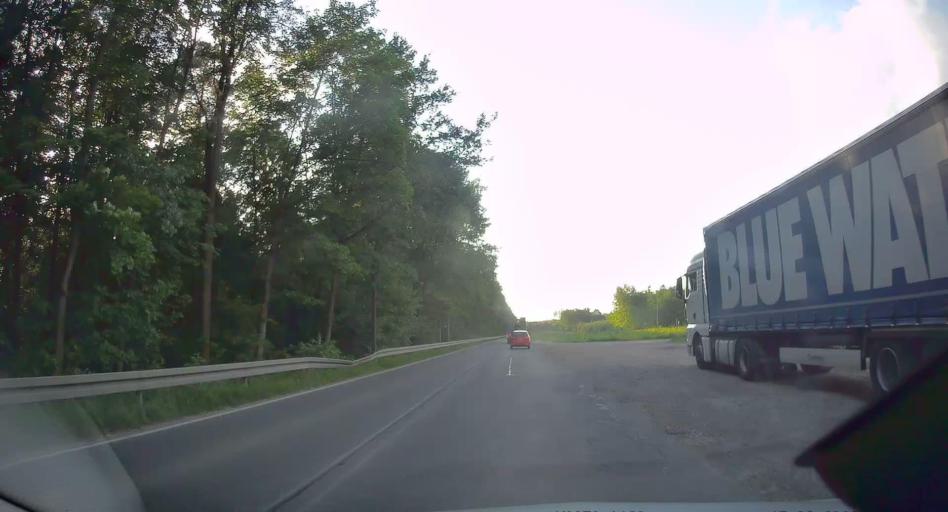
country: PL
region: Silesian Voivodeship
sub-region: Powiat bierunsko-ledzinski
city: Imielin
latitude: 50.1615
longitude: 19.1753
